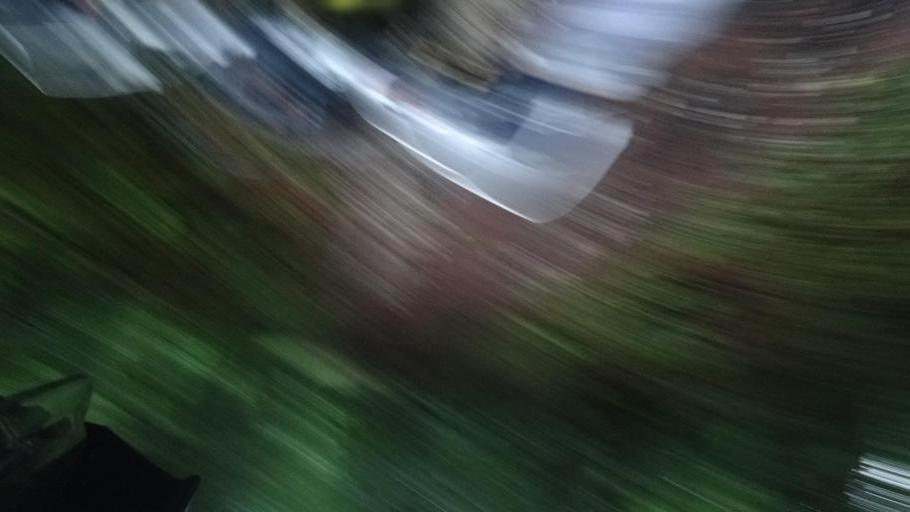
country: HR
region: Licko-Senjska
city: Jezerce
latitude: 44.8216
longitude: 15.6181
